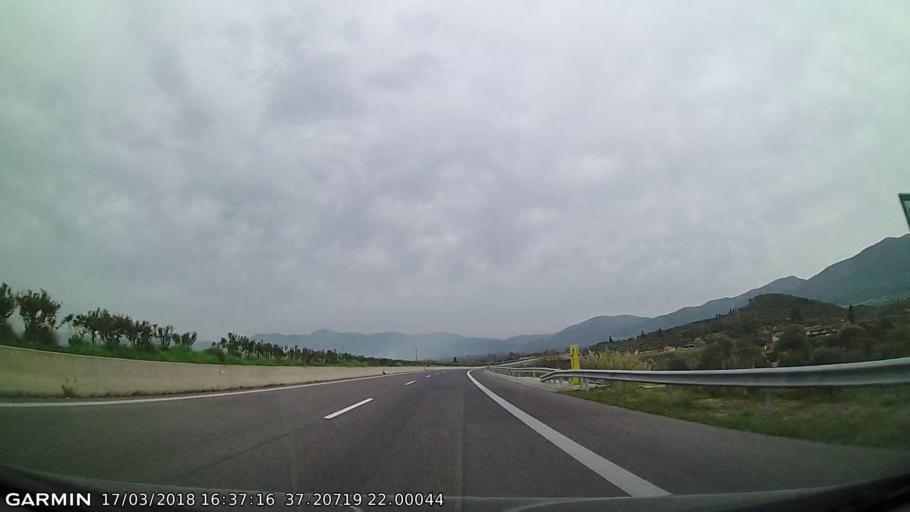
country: GR
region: Peloponnese
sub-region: Nomos Messinias
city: Meligalas
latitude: 37.2081
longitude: 22.0005
